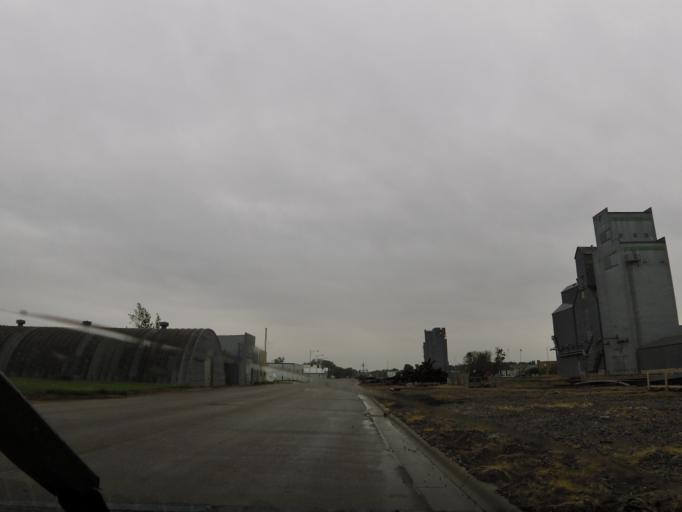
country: US
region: Minnesota
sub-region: Marshall County
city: Warren
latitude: 48.4527
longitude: -96.8738
